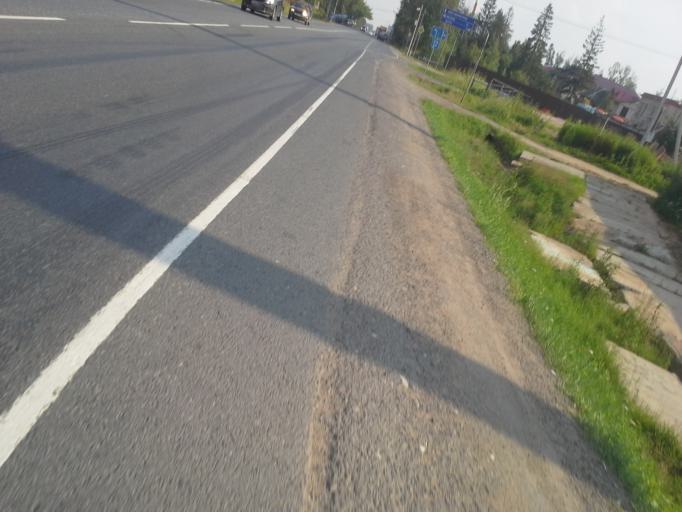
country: RU
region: Moskovskaya
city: Istra
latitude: 55.9073
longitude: 36.9452
